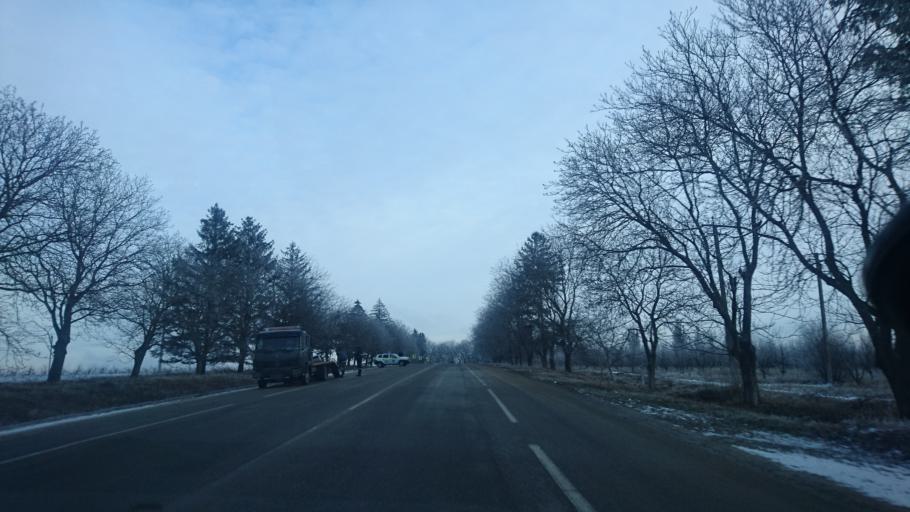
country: MD
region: Briceni
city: Briceni
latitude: 48.2841
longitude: 27.1440
